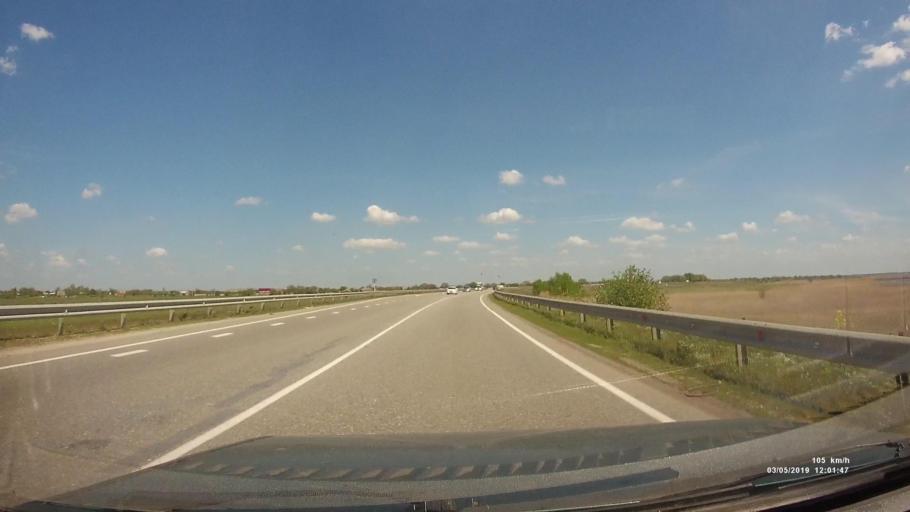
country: RU
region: Rostov
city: Bagayevskaya
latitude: 47.2675
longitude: 40.3544
